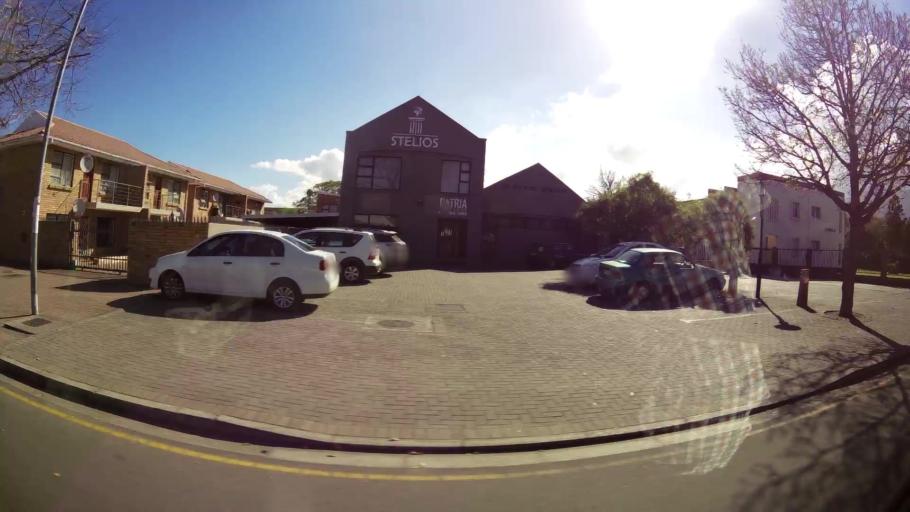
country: ZA
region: Western Cape
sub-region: Eden District Municipality
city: George
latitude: -33.9648
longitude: 22.4562
